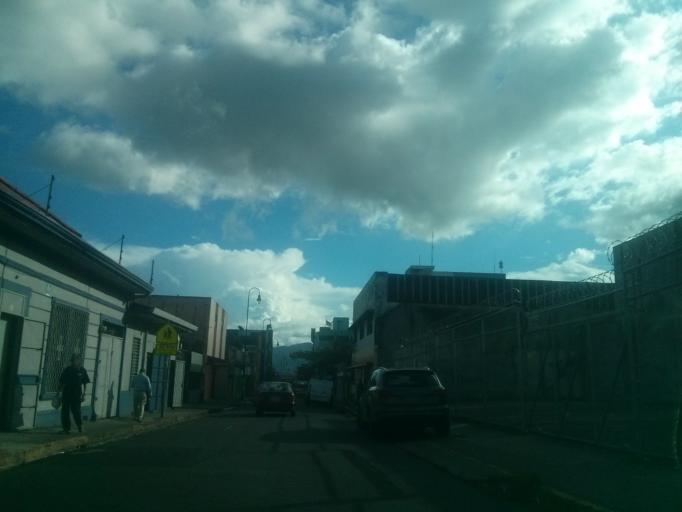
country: CR
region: San Jose
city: San Jose
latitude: 9.9297
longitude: -84.0785
